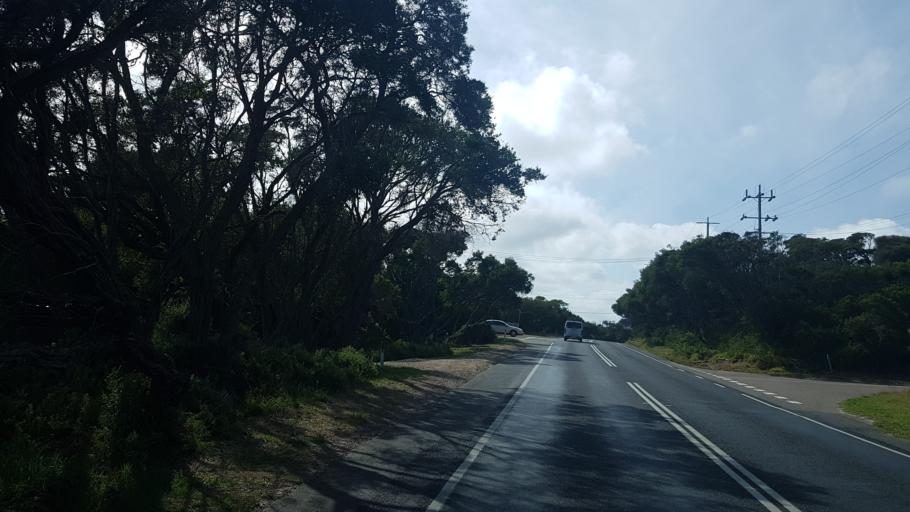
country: AU
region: Victoria
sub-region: Mornington Peninsula
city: Blairgowrie
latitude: -38.3633
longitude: 144.7634
